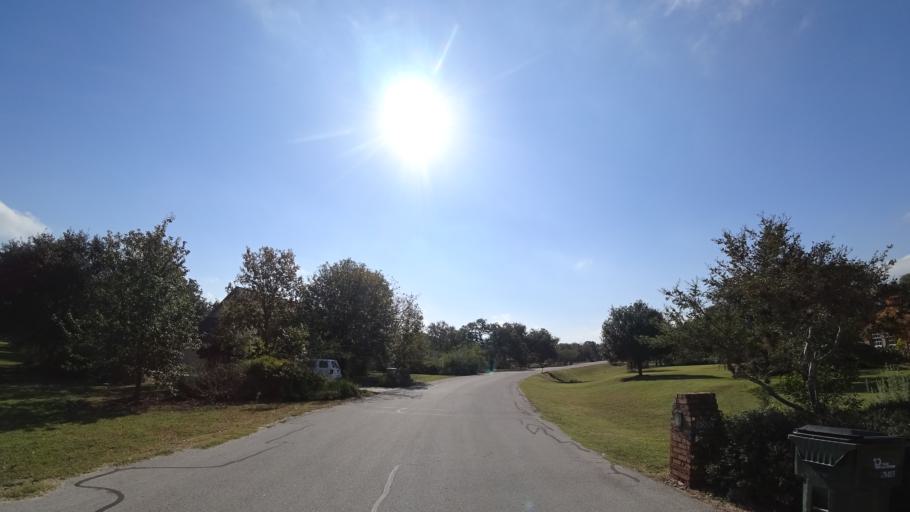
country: US
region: Texas
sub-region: Travis County
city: Shady Hollow
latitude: 30.1595
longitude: -97.8676
